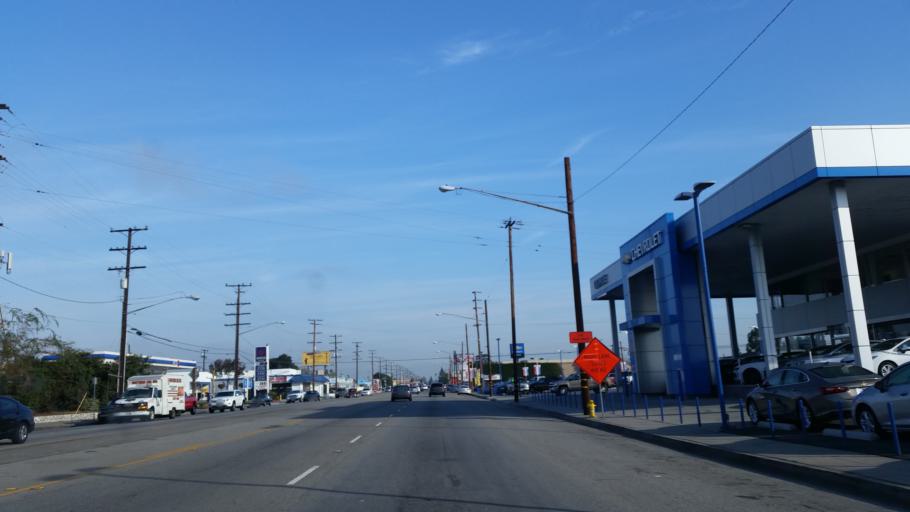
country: US
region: California
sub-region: Los Angeles County
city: Paramount
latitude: 33.8789
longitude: -118.1425
